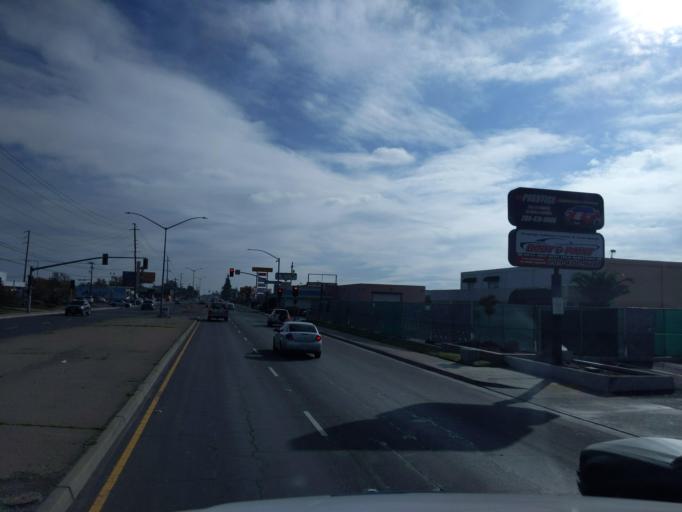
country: US
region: California
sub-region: San Joaquin County
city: August
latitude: 37.9909
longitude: -121.2865
